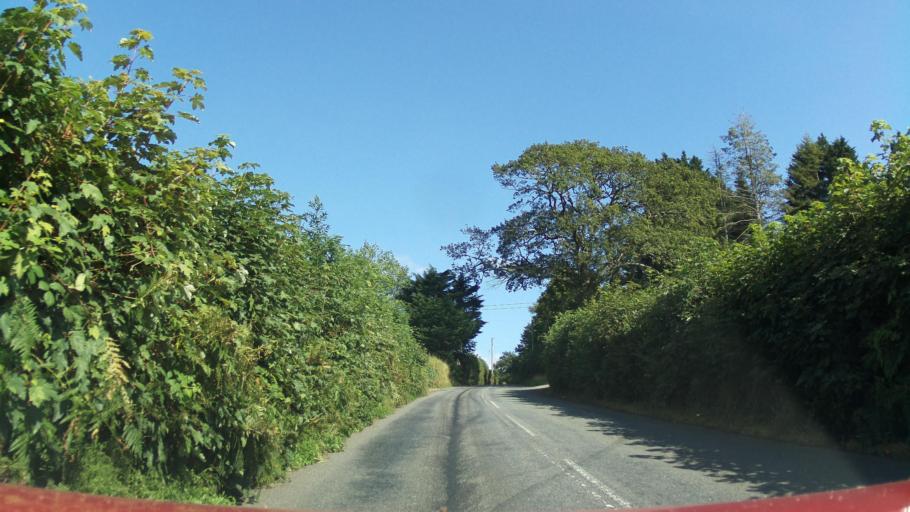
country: GB
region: England
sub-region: Devon
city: Tavistock
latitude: 50.5526
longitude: -4.1243
